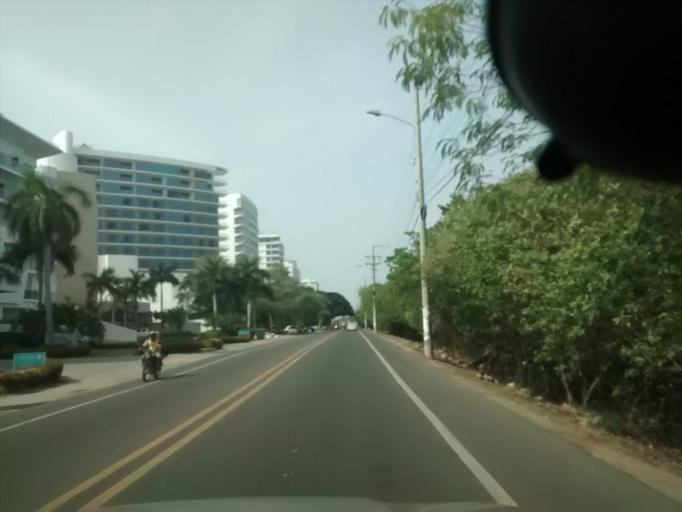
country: CO
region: Bolivar
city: Cartagena
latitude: 10.4626
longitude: -75.5033
